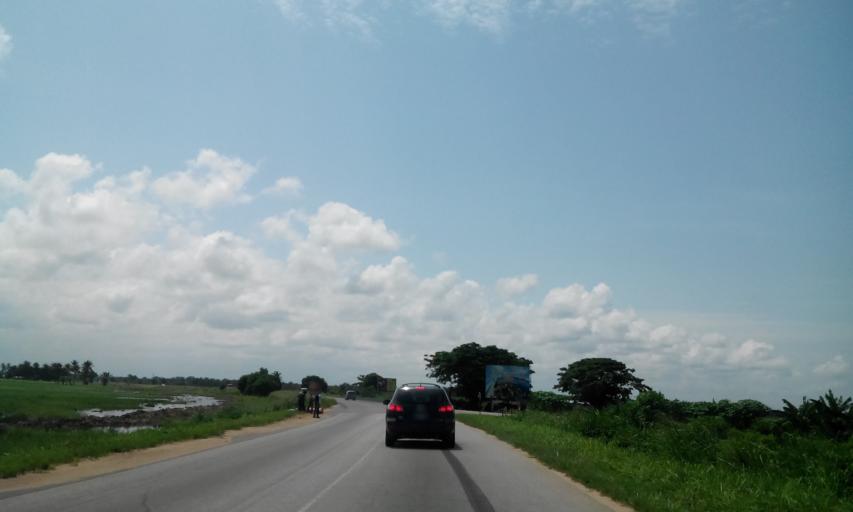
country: CI
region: Sud-Comoe
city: Grand-Bassam
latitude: 5.2144
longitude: -3.7075
